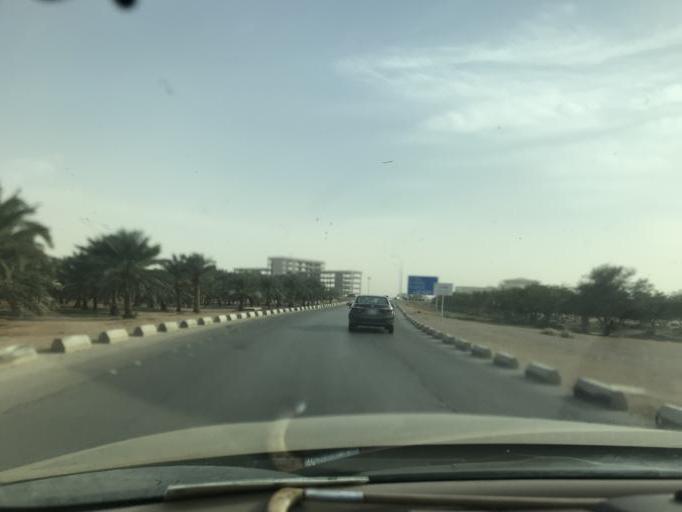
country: SA
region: Ar Riyad
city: Riyadh
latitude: 24.9307
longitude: 46.7152
